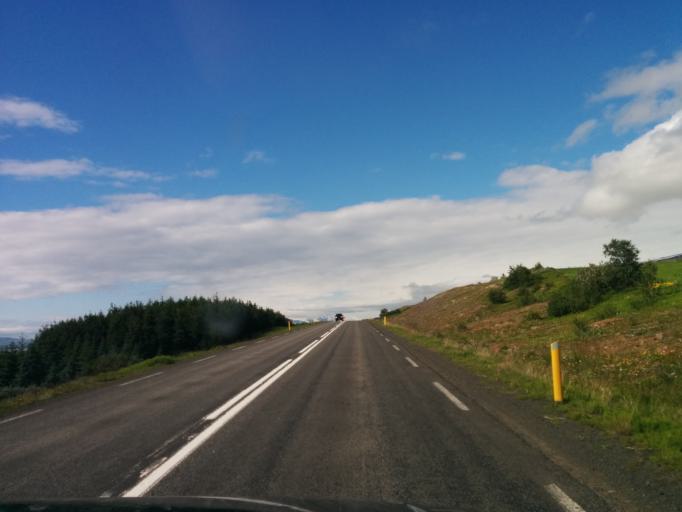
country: IS
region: Northeast
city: Akureyri
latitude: 65.7299
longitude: -18.0738
